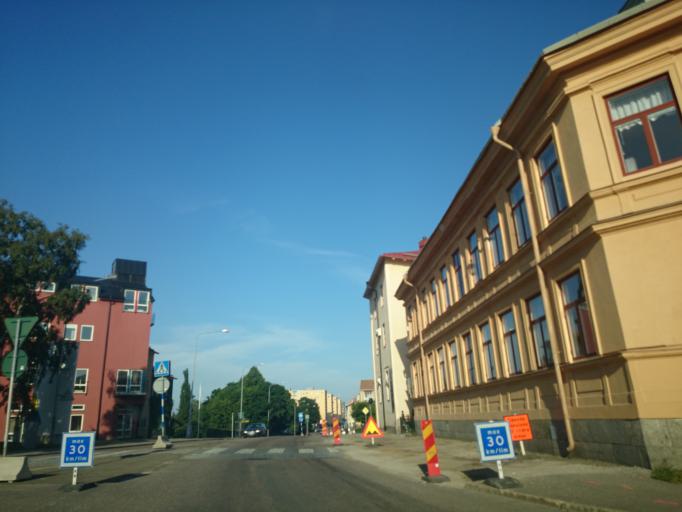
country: SE
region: Vaesternorrland
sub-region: Sundsvalls Kommun
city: Sundsvall
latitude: 62.3931
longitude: 17.2829
